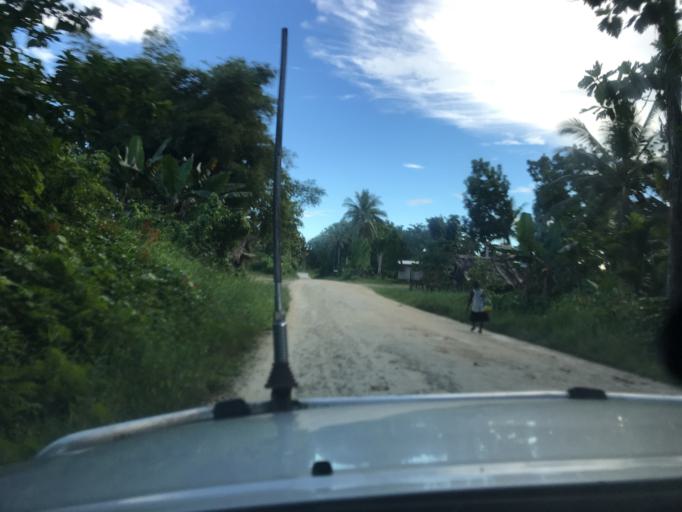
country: SB
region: Malaita
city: Auki
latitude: -8.6842
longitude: 160.6911
